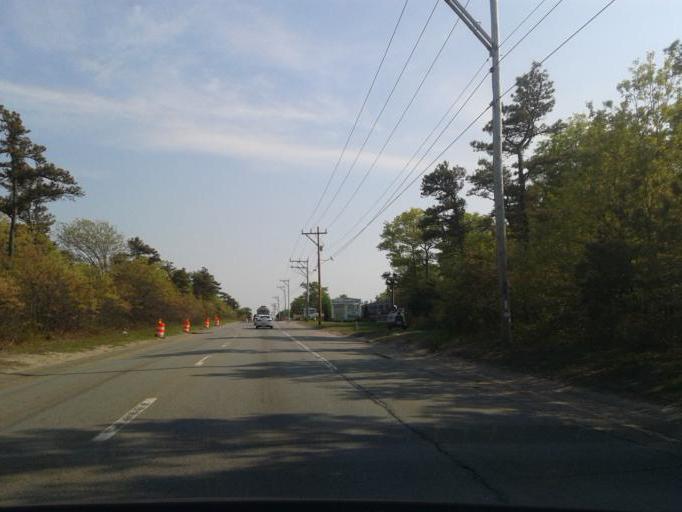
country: US
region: Massachusetts
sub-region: Barnstable County
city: Monument Beach
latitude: 41.7093
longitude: -70.5835
